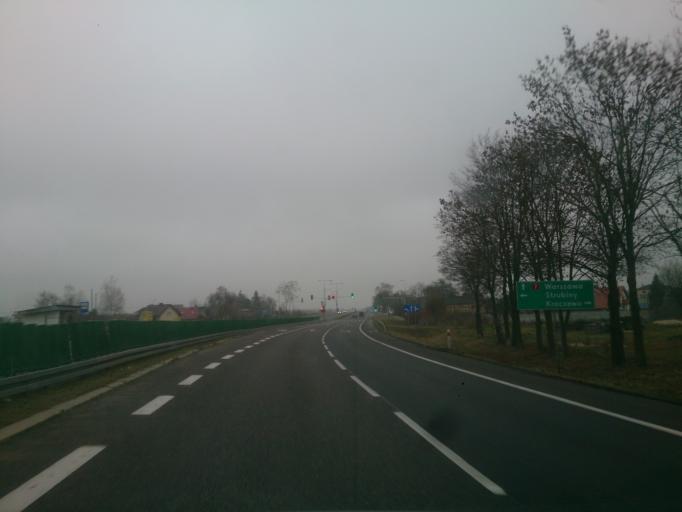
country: PL
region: Masovian Voivodeship
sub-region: Powiat plonski
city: Zaluski
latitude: 52.4781
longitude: 20.5629
